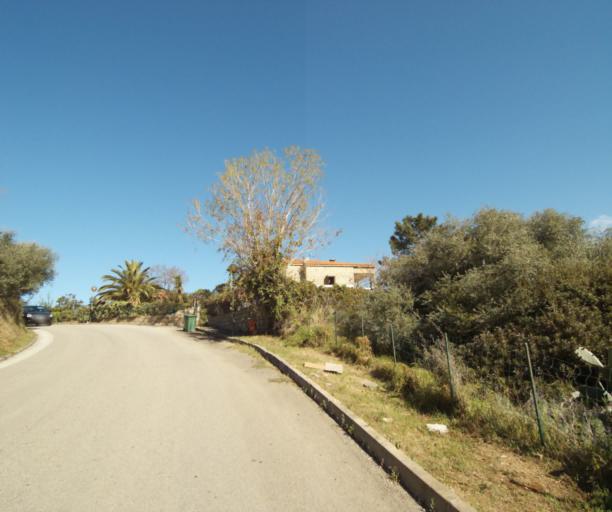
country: FR
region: Corsica
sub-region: Departement de la Corse-du-Sud
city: Propriano
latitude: 41.6692
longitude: 8.9006
